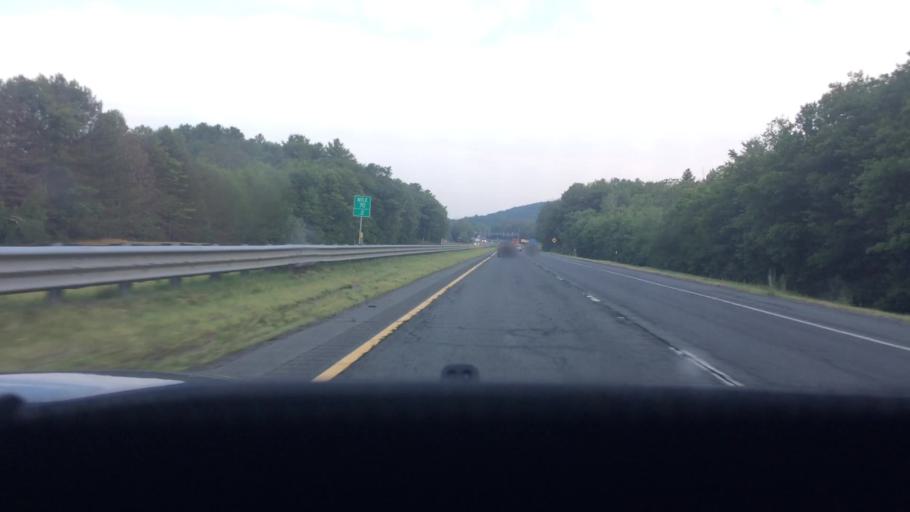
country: US
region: Massachusetts
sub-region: Worcester County
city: Warren
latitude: 42.1767
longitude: -72.1981
